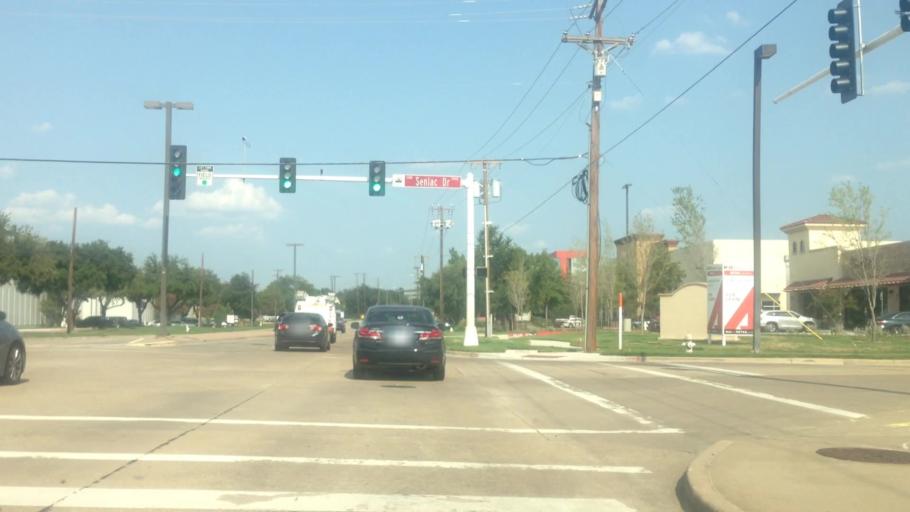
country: US
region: Texas
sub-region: Dallas County
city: Farmers Branch
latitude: 32.9223
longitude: -96.9098
